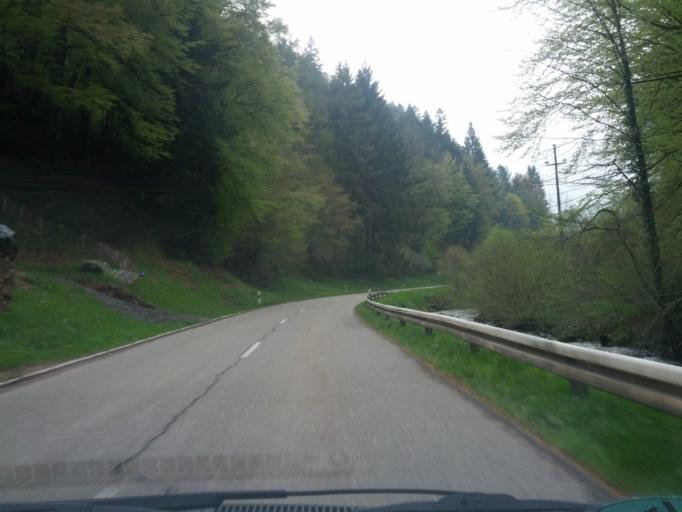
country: DE
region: Baden-Wuerttemberg
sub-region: Freiburg Region
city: Zell im Wiesental
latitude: 47.7327
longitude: 7.8049
